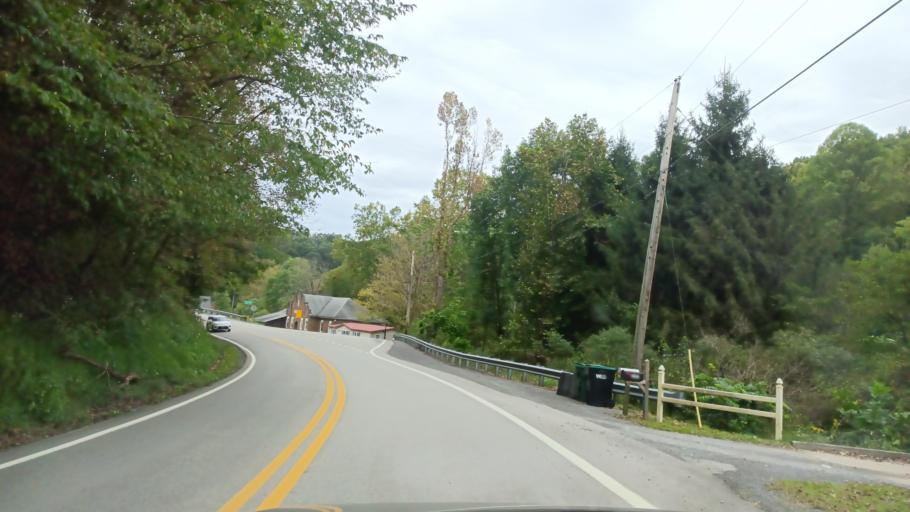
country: US
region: West Virginia
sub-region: Taylor County
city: Grafton
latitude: 39.3445
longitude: -79.9386
